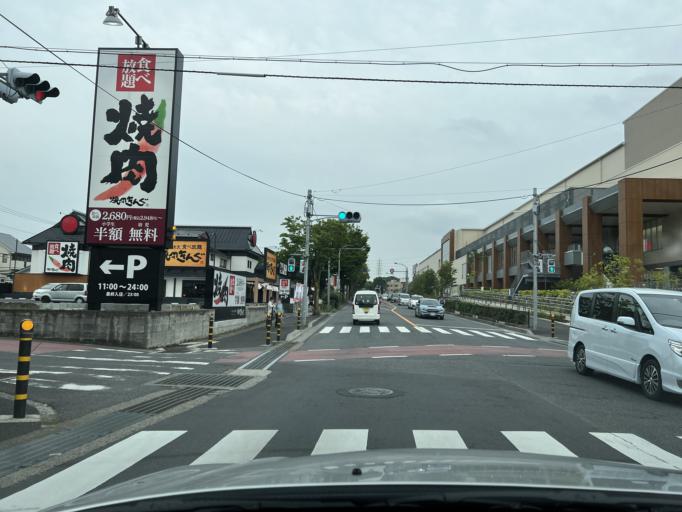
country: JP
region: Chiba
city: Nagareyama
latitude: 35.8192
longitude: 139.9331
